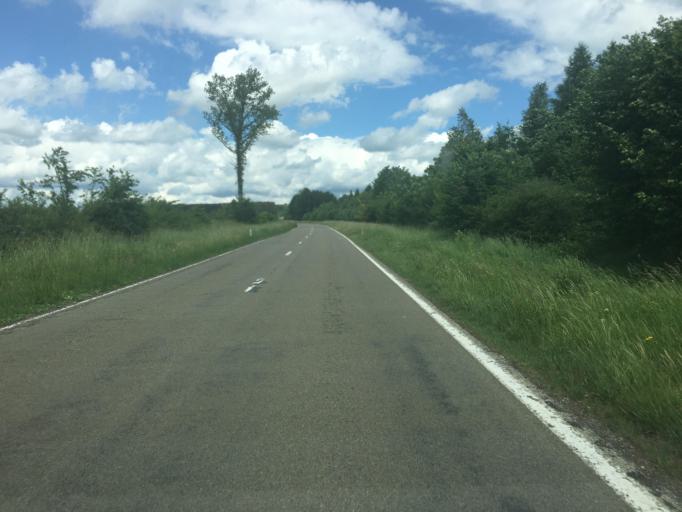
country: BE
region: Wallonia
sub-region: Province du Luxembourg
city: Florenville
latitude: 49.6518
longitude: 5.3380
